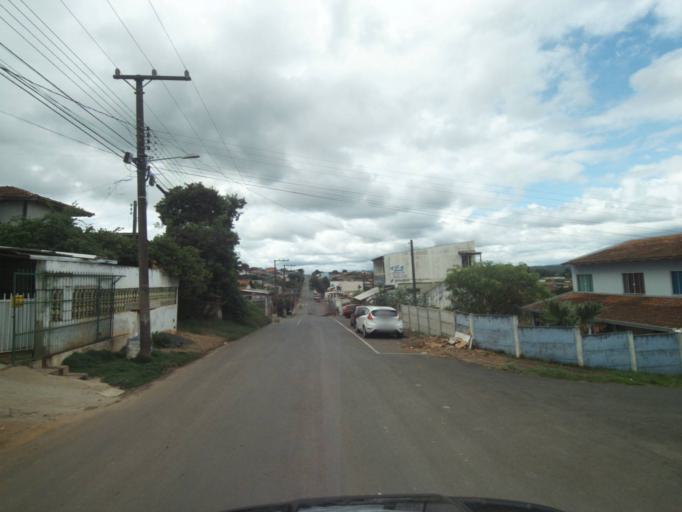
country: BR
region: Parana
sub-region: Telemaco Borba
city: Telemaco Borba
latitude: -24.3171
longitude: -50.6493
